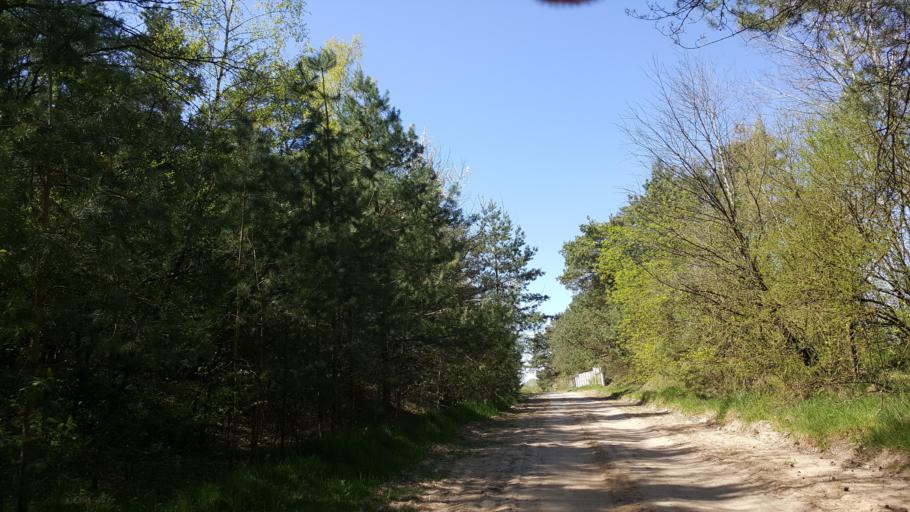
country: BY
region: Brest
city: Charnawchytsy
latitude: 52.3266
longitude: 23.6646
